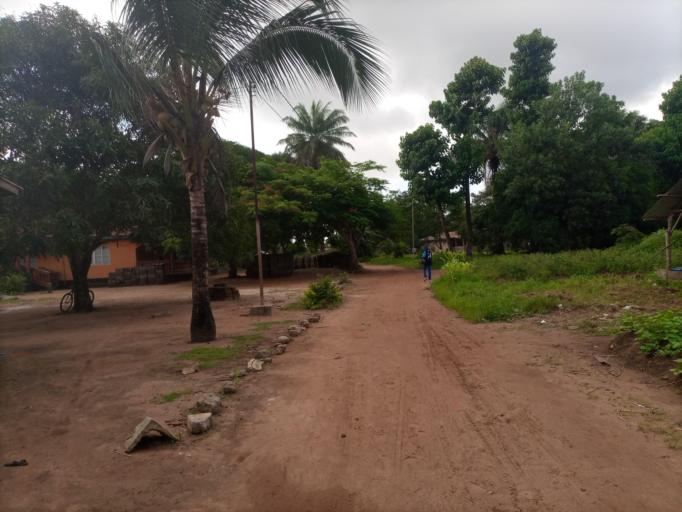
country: SL
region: Northern Province
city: Sawkta
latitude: 8.6395
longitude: -13.2121
